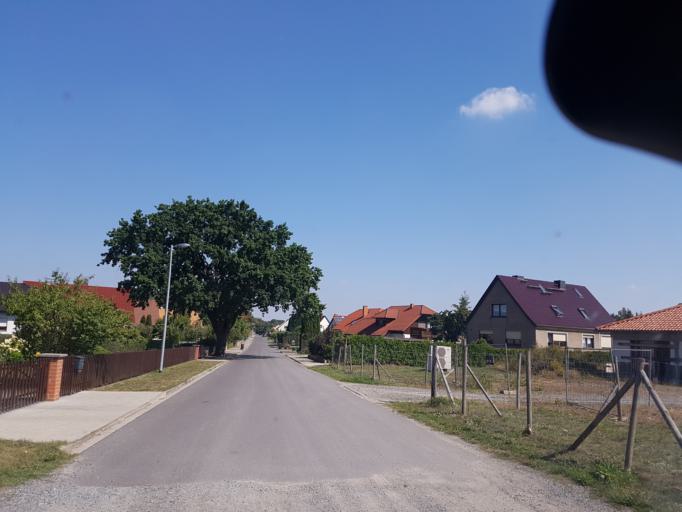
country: DE
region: Brandenburg
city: Elsterwerda
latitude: 51.4912
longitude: 13.5015
